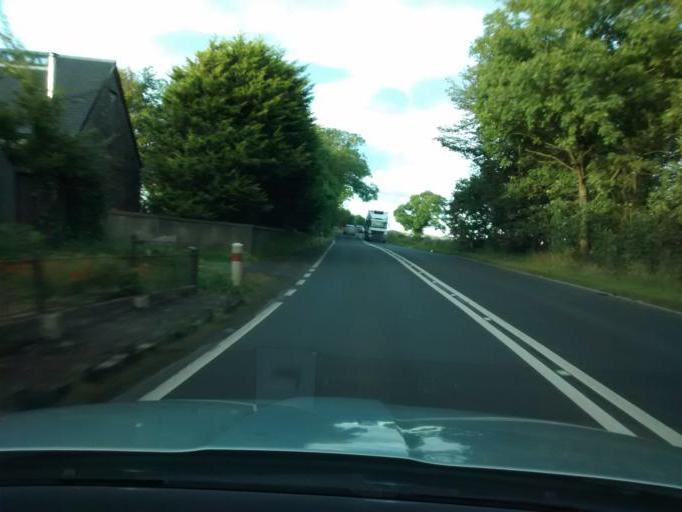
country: GB
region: Scotland
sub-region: Renfrewshire
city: Lochwinnoch
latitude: 55.7975
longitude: -4.5948
